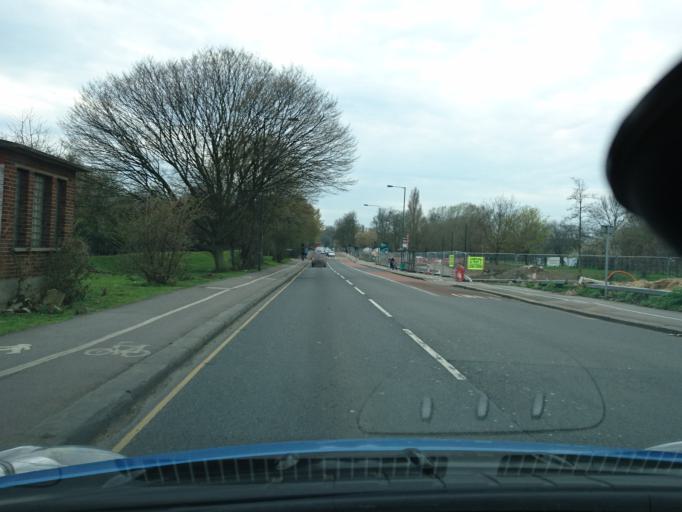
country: GB
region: England
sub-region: Greater London
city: Hackney
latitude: 51.5651
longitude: -0.0389
